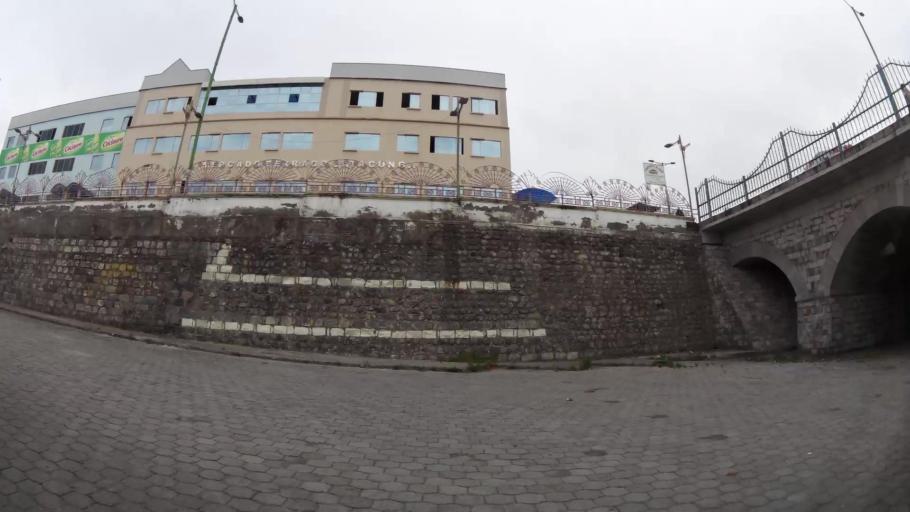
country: EC
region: Cotopaxi
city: Latacunga
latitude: -0.9321
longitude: -78.6201
